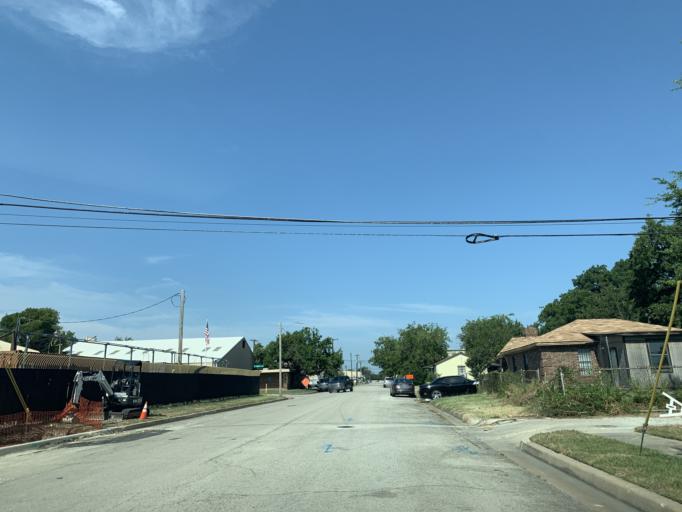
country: US
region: Texas
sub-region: Tarrant County
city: Fort Worth
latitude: 32.7078
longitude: -97.3225
